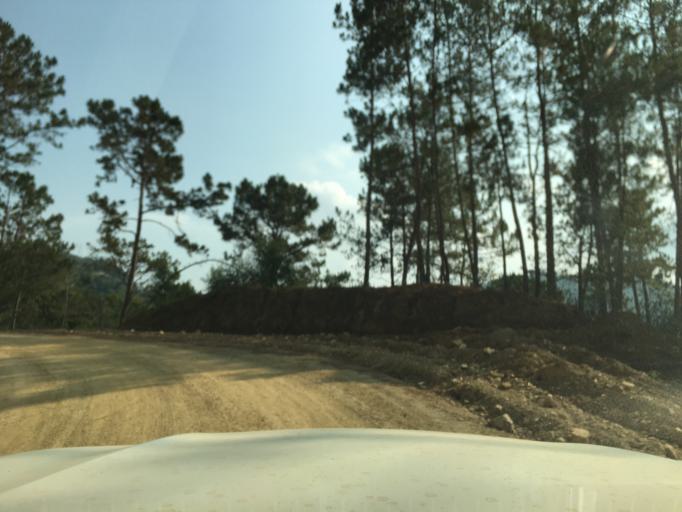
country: LA
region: Houaphan
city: Huameung
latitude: 20.1941
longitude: 103.8326
